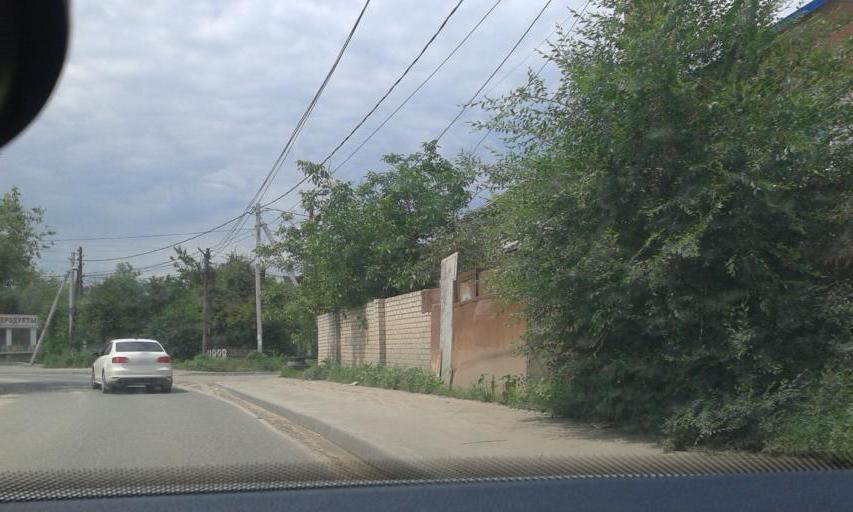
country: RU
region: Volgograd
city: Gorodishche
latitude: 48.7724
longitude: 44.4949
